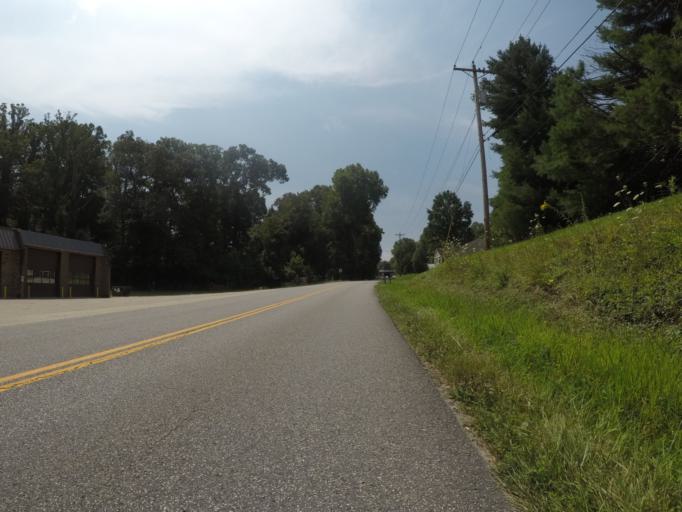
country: US
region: Kentucky
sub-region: Boyd County
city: Ironville
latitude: 38.4431
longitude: -82.7089
